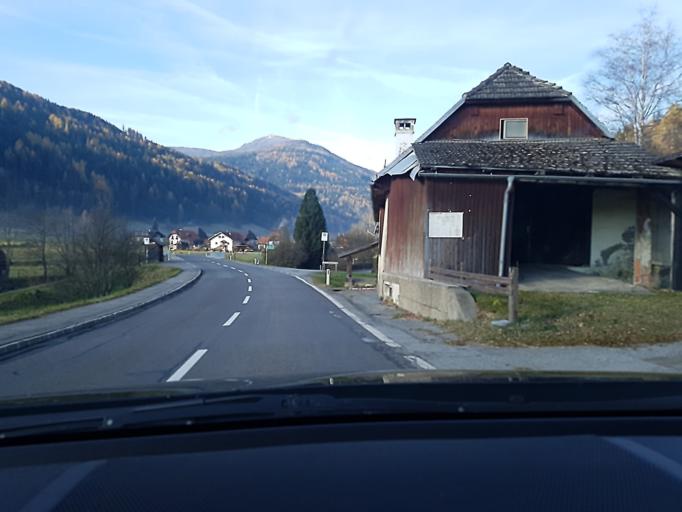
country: AT
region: Styria
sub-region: Politischer Bezirk Murau
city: Ranten
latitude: 47.1600
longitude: 14.0662
